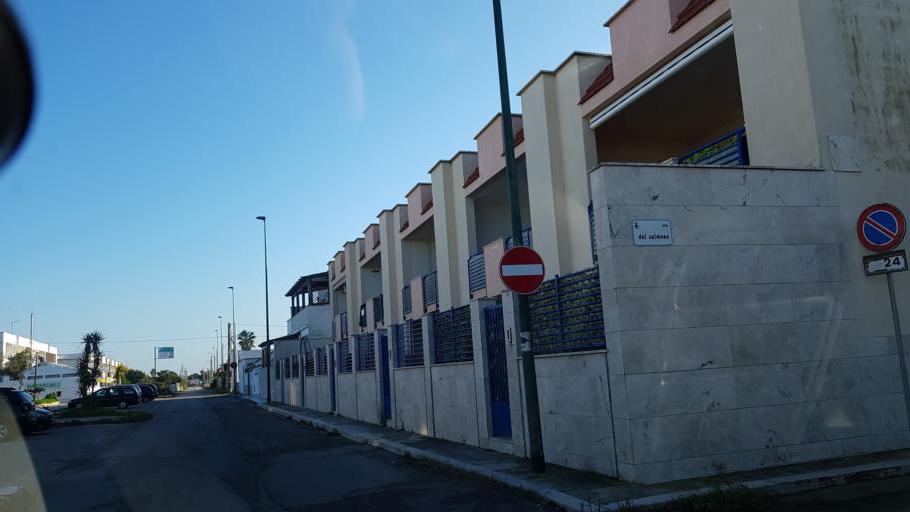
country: IT
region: Apulia
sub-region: Provincia di Brindisi
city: Torchiarolo
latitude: 40.5168
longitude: 18.0926
